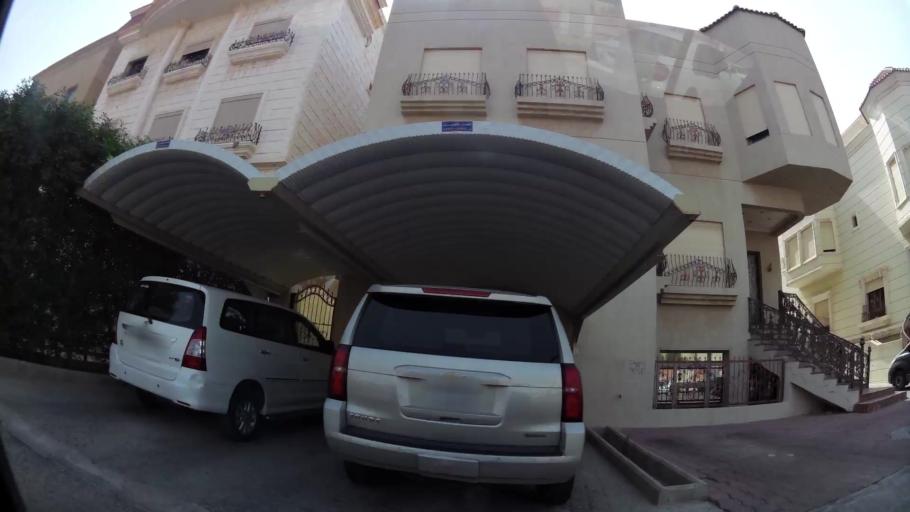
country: KW
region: Muhafazat al Jahra'
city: Al Jahra'
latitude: 29.3069
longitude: 47.6903
